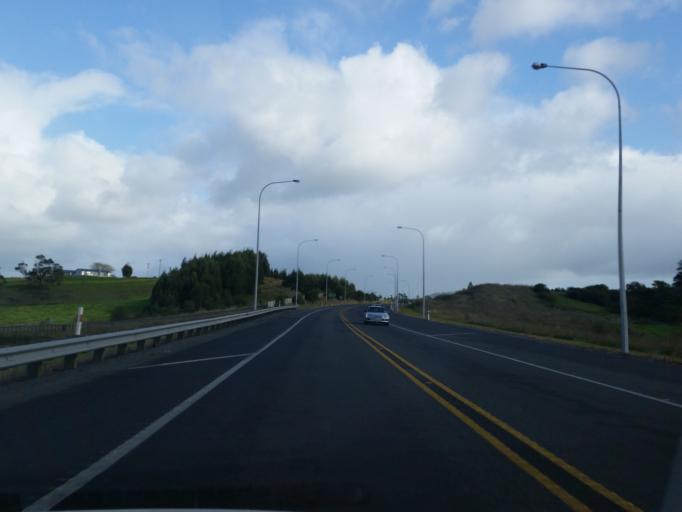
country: NZ
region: Auckland
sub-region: Auckland
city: Pukekohe East
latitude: -37.2209
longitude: 175.1242
